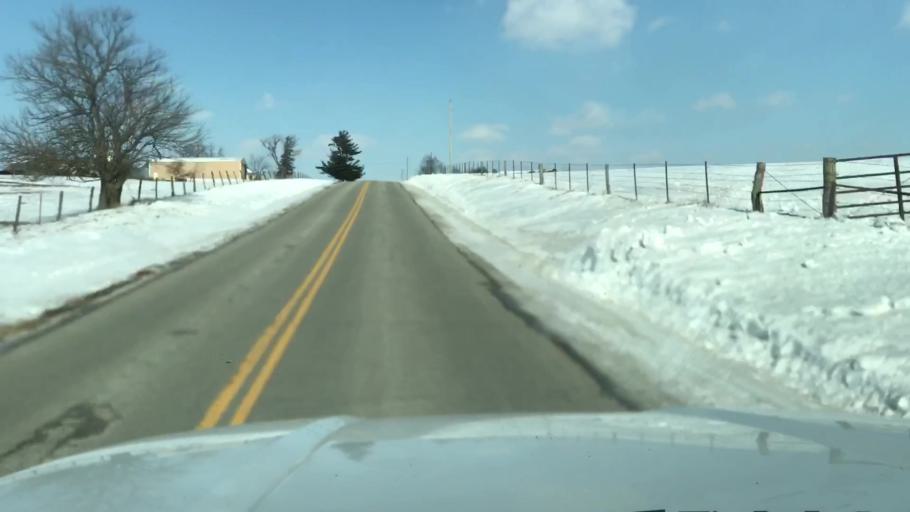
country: US
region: Missouri
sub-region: Nodaway County
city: Maryville
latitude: 40.3799
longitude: -94.7215
